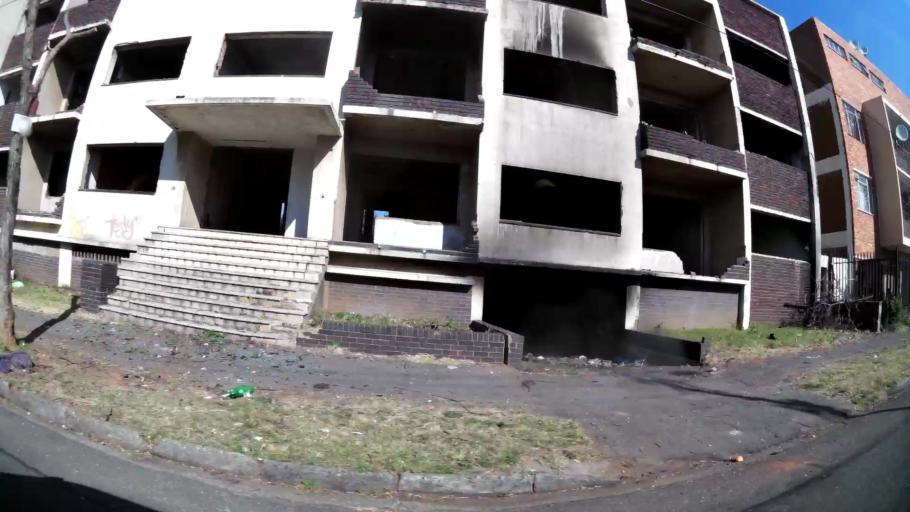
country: ZA
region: Gauteng
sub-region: City of Johannesburg Metropolitan Municipality
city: Johannesburg
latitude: -26.1855
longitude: 28.0699
